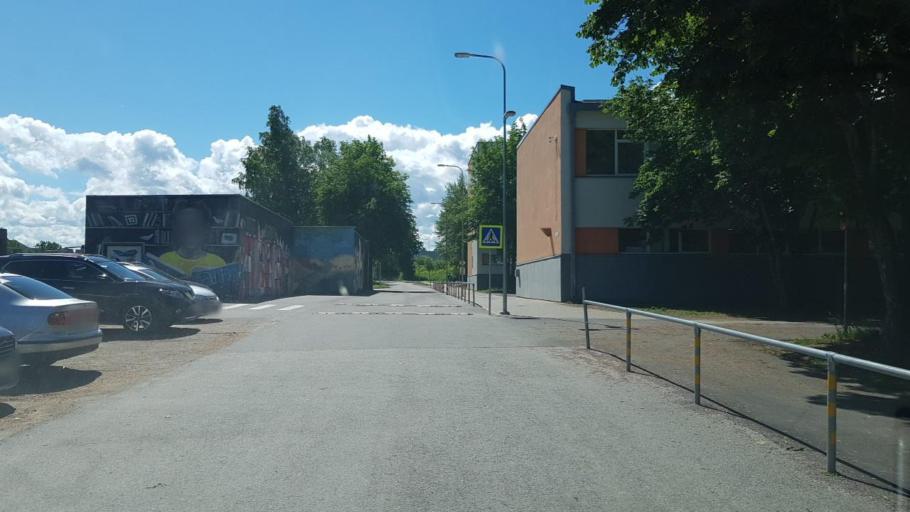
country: EE
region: Ida-Virumaa
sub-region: Narva linn
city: Narva
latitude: 59.3853
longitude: 28.1713
